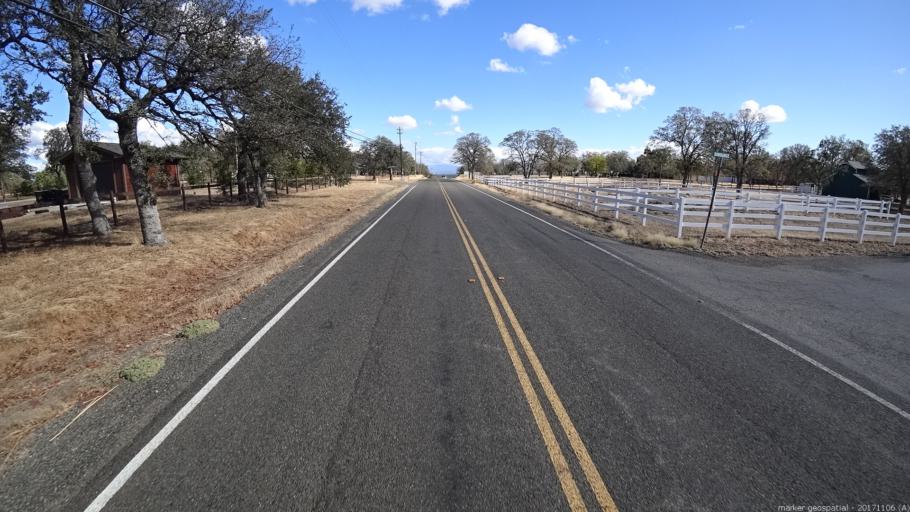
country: US
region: California
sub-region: Shasta County
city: Palo Cedro
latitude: 40.5928
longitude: -122.2554
